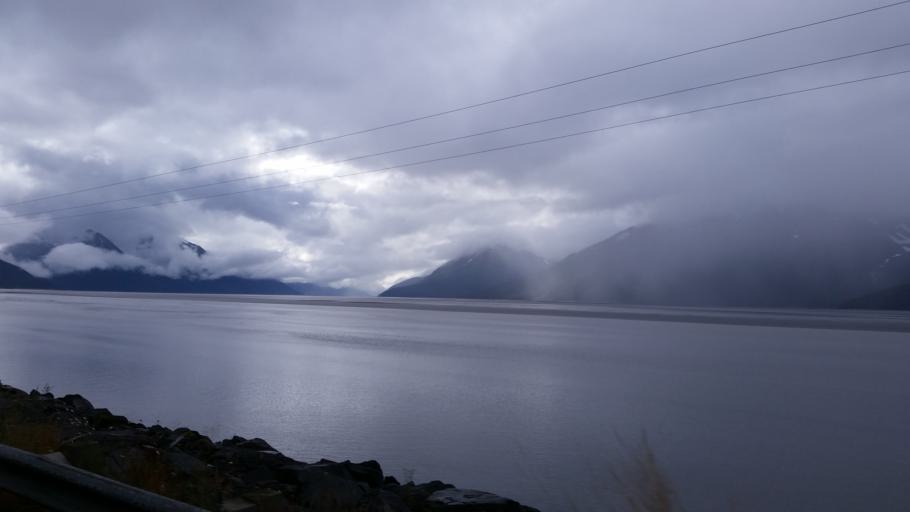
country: US
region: Alaska
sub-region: Anchorage Municipality
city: Girdwood
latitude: 60.9366
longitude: -149.2849
